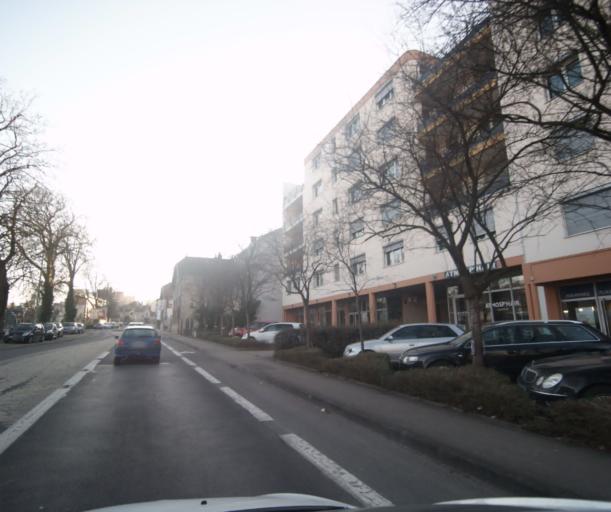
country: FR
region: Franche-Comte
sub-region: Departement du Doubs
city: Besancon
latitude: 47.2409
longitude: 6.0142
